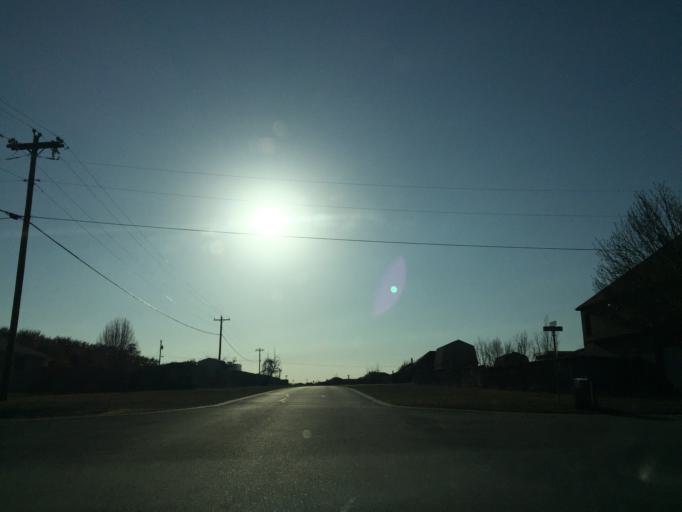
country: US
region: Texas
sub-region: Williamson County
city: Florence
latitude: 30.7530
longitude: -97.8104
